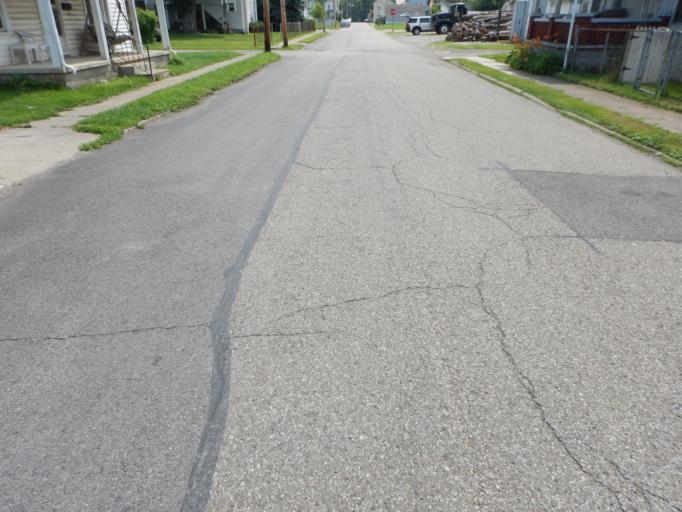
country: US
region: Ohio
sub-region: Muskingum County
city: Zanesville
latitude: 39.9214
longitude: -82.0074
